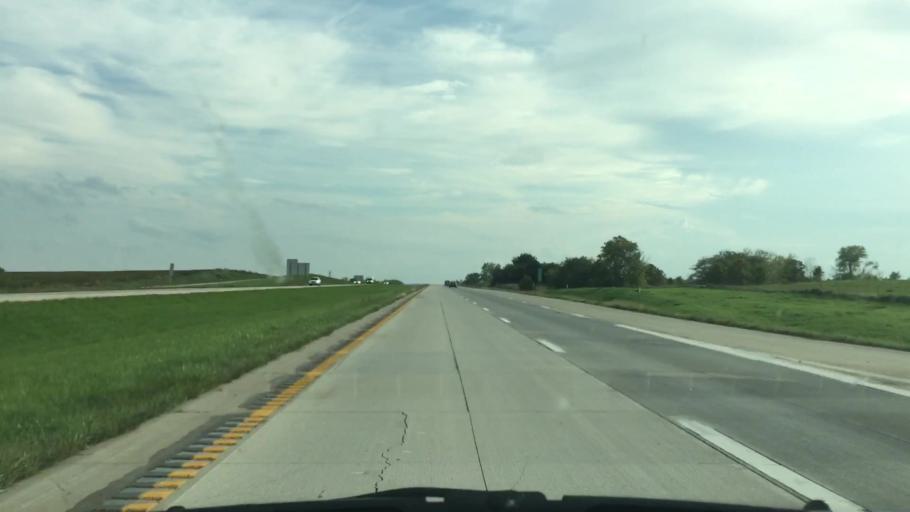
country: US
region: Missouri
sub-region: Harrison County
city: Bethany
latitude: 40.0740
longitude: -94.0937
